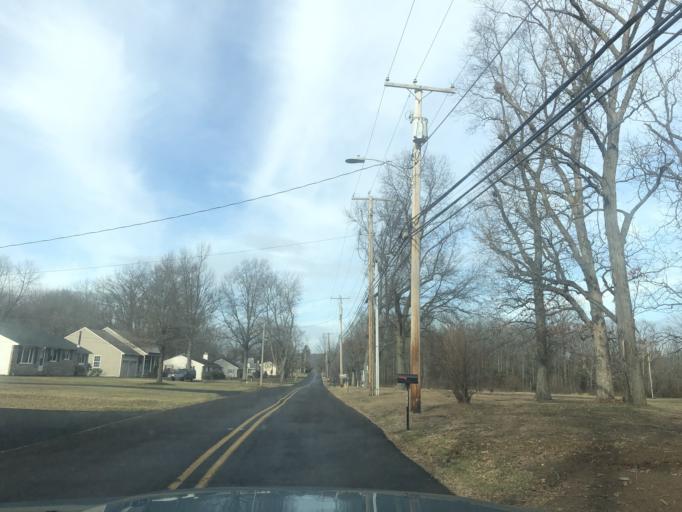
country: US
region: Pennsylvania
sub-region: Bucks County
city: Perkasie
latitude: 40.3812
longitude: -75.2961
